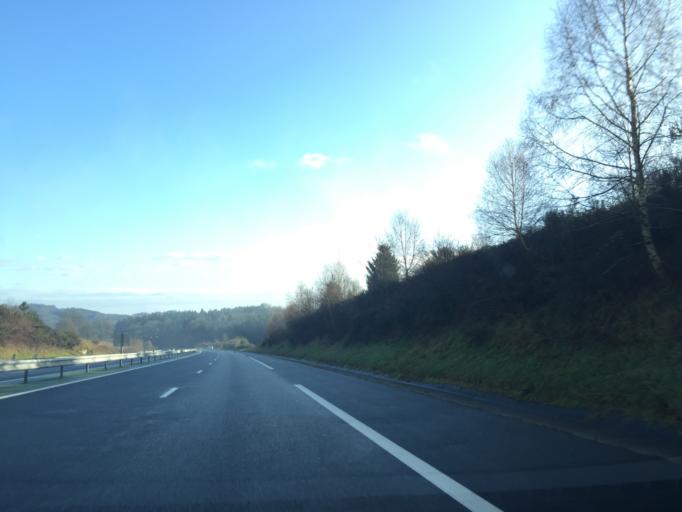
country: FR
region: Limousin
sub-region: Departement de la Correze
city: Saint-Clement
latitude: 45.3095
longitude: 1.7026
